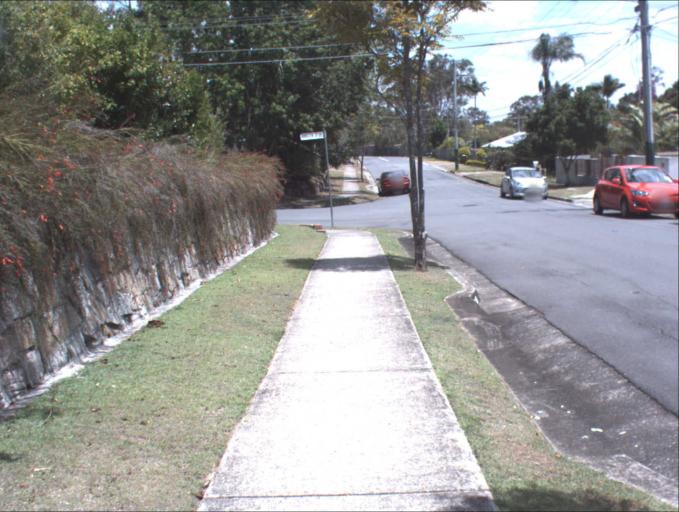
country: AU
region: Queensland
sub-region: Logan
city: Slacks Creek
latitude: -27.6406
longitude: 153.1628
